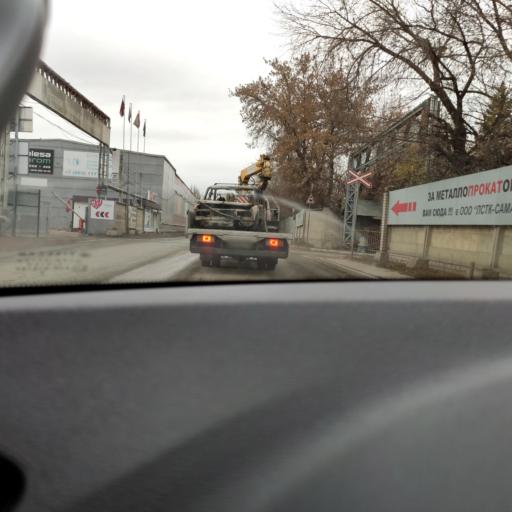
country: RU
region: Samara
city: Smyshlyayevka
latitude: 53.2086
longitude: 50.3013
